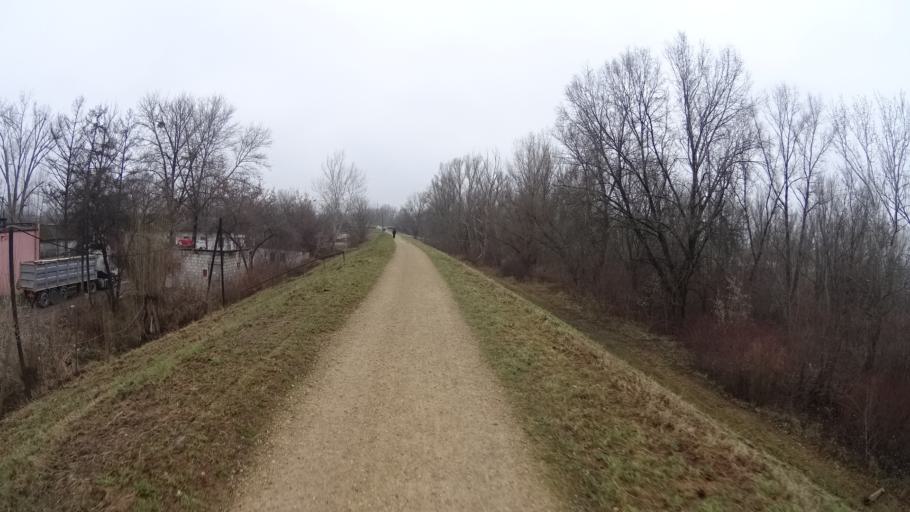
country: PL
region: Masovian Voivodeship
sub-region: Warszawa
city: Praga Poludnie
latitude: 52.2091
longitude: 21.0920
